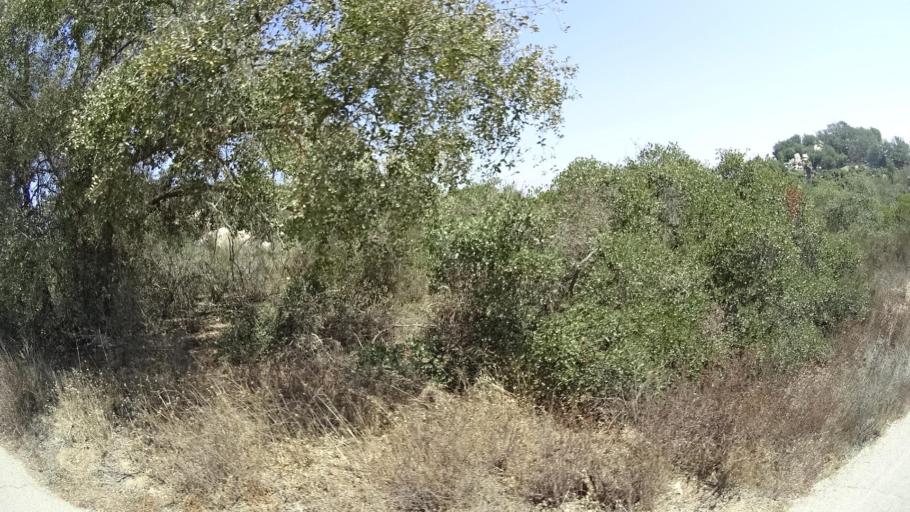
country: US
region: California
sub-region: San Diego County
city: Fallbrook
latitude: 33.4286
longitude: -117.2753
